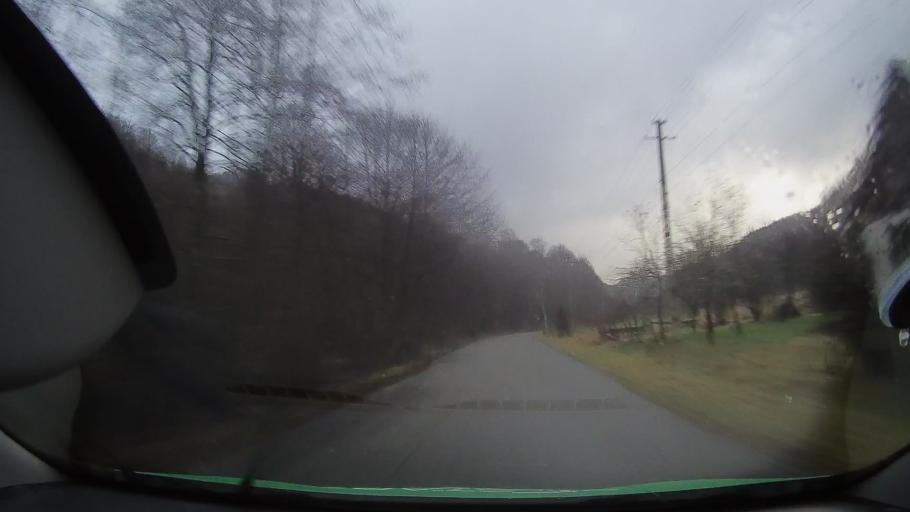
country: RO
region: Hunedoara
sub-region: Comuna Ribita
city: Ribita
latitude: 46.2634
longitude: 22.7430
